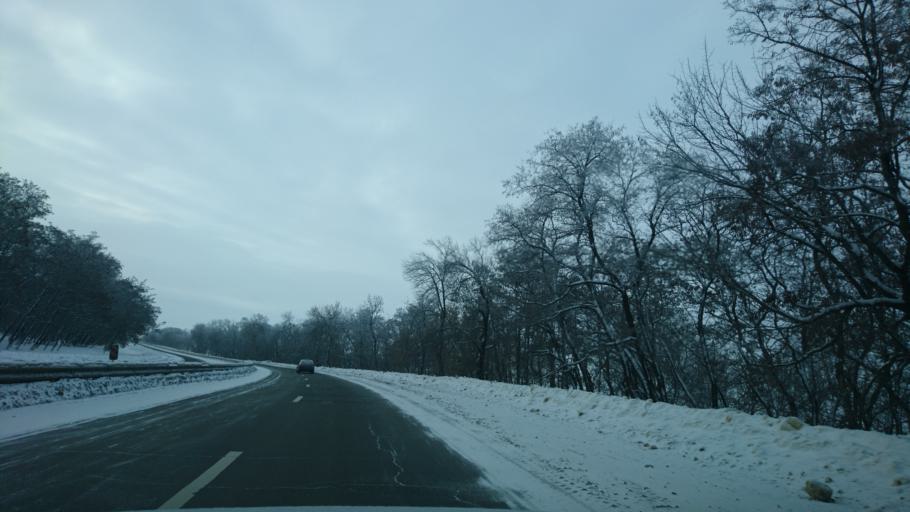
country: RU
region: Belgorod
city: Mayskiy
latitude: 50.4827
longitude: 36.4070
